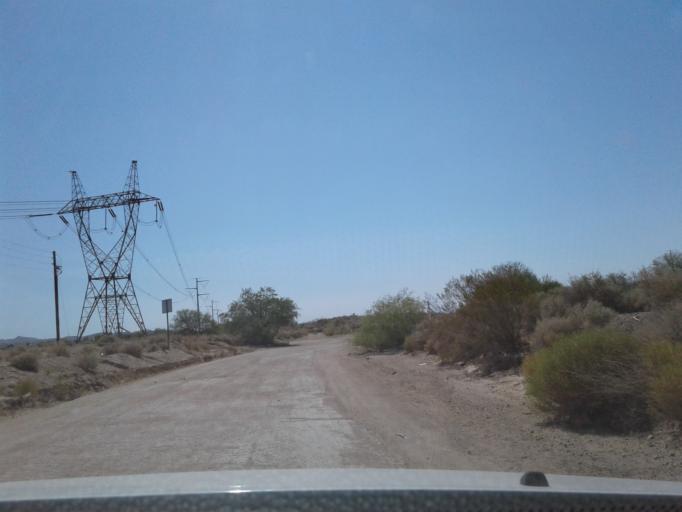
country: US
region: Arizona
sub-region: Maricopa County
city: Laveen
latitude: 33.2904
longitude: -112.1346
